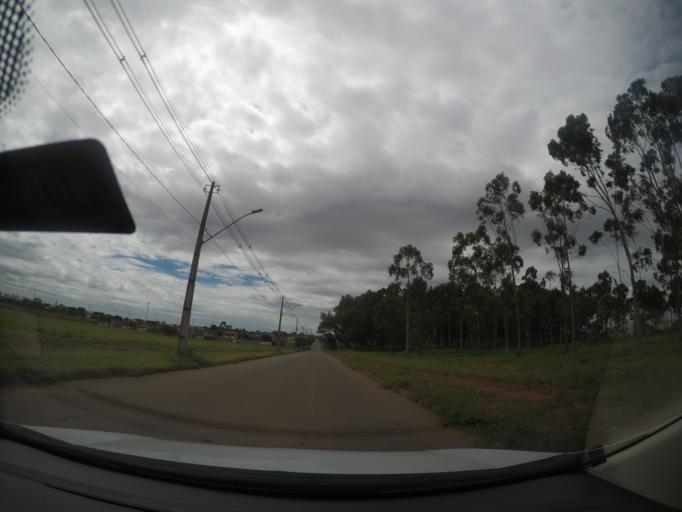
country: BR
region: Goias
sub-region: Goiania
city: Goiania
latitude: -16.7259
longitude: -49.3465
